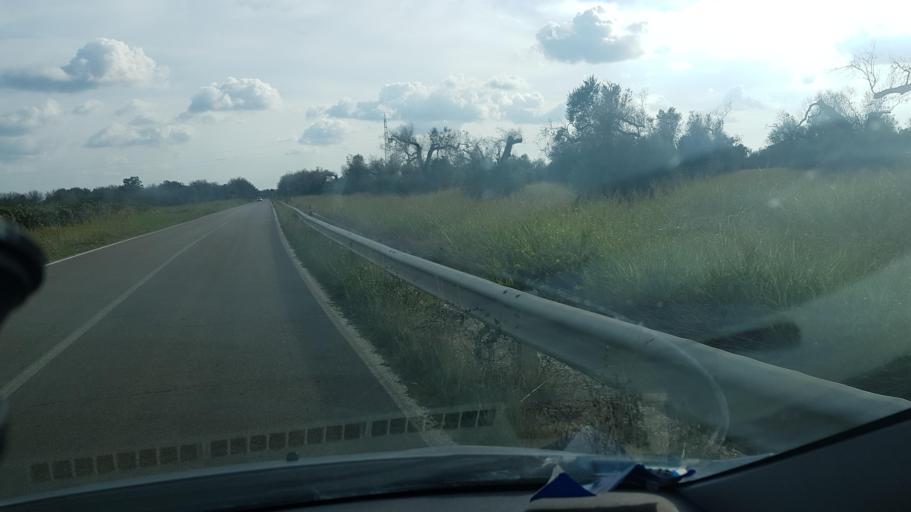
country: IT
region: Apulia
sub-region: Provincia di Brindisi
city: Cellino San Marco
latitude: 40.4499
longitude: 17.9549
